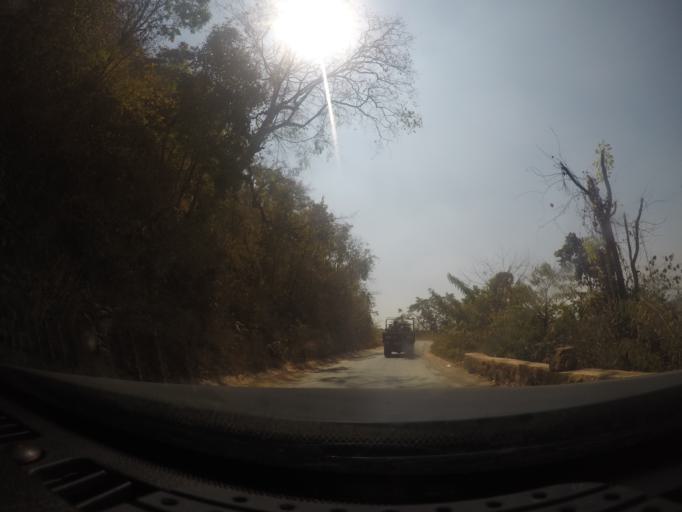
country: MM
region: Shan
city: Taunggyi
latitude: 20.8169
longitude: 97.2243
